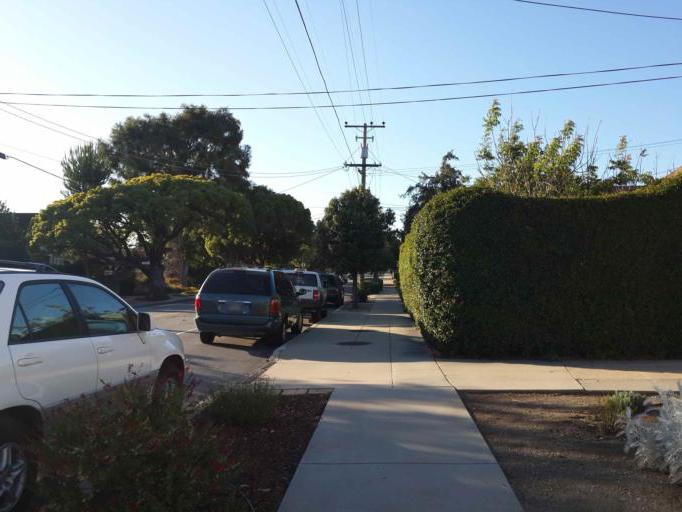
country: US
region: California
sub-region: San Luis Obispo County
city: San Luis Obispo
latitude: 35.2860
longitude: -120.6681
